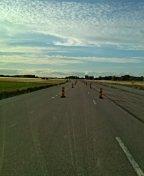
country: SE
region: Uppsala
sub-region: Enkopings Kommun
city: Irsta
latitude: 59.7452
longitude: 16.9490
